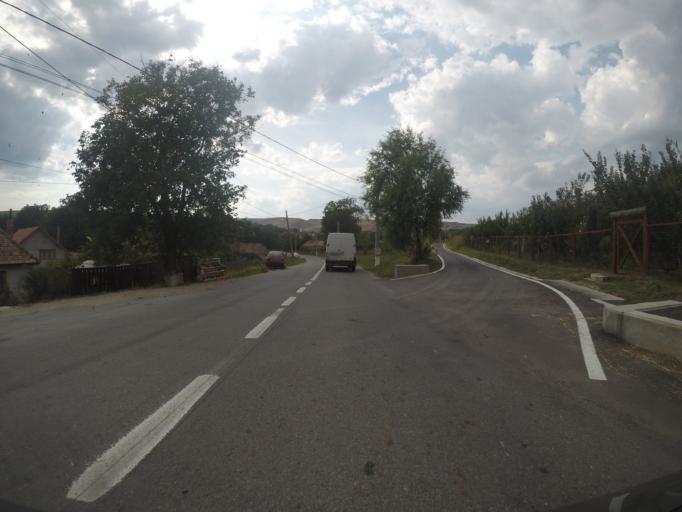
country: RO
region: Cluj
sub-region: Comuna Sandulesti
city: Sandulesti
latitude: 46.5804
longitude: 23.7297
